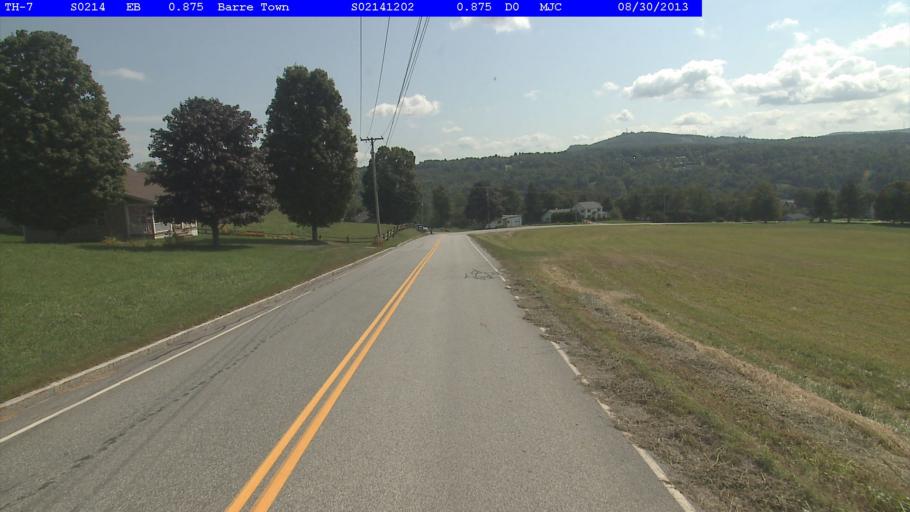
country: US
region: Vermont
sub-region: Washington County
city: South Barre
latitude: 44.1810
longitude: -72.5120
